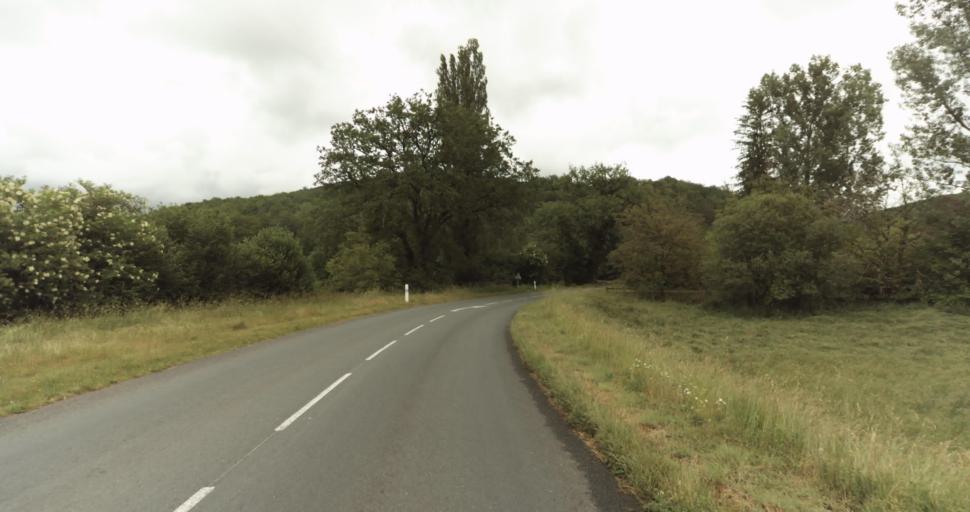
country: FR
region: Aquitaine
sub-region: Departement de la Dordogne
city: Beaumont-du-Perigord
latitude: 44.7705
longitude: 0.7966
